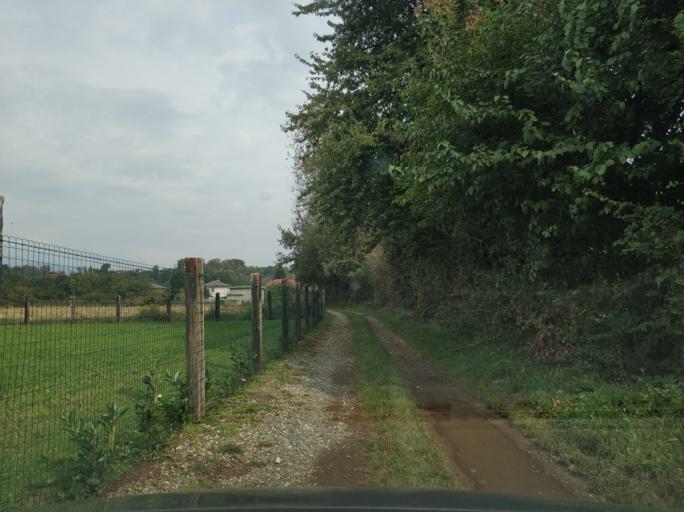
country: IT
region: Piedmont
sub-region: Provincia di Torino
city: Nole
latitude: 45.2531
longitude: 7.5694
